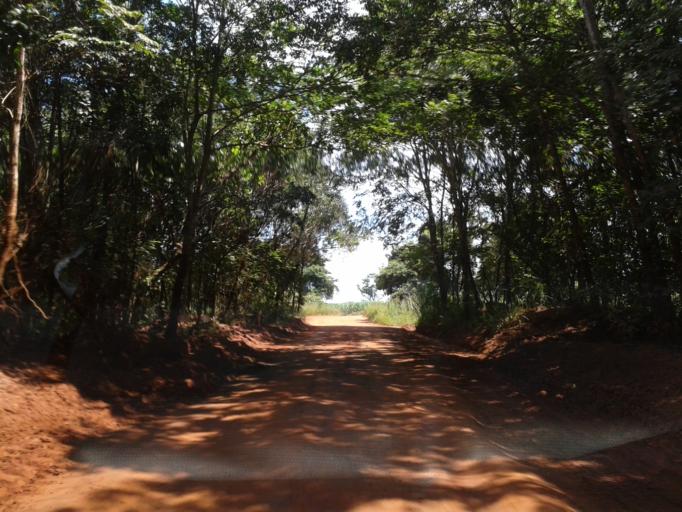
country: BR
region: Minas Gerais
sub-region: Ituiutaba
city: Ituiutaba
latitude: -19.0851
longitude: -49.7340
